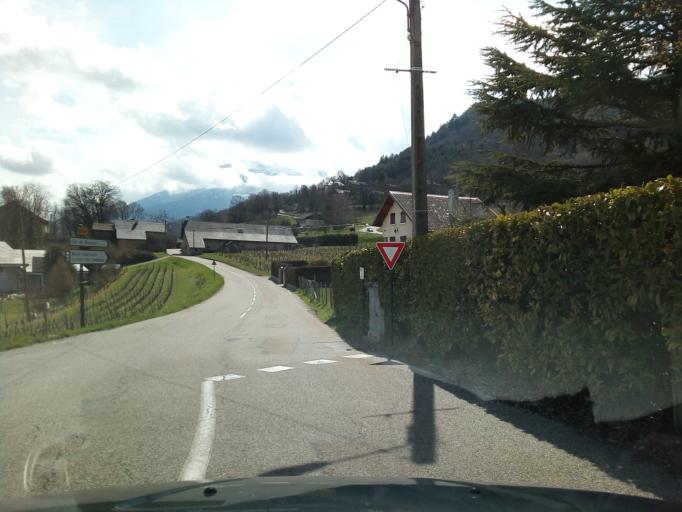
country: FR
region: Rhone-Alpes
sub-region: Departement de la Savoie
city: Saint-Baldoph
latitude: 45.5370
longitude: 5.9474
